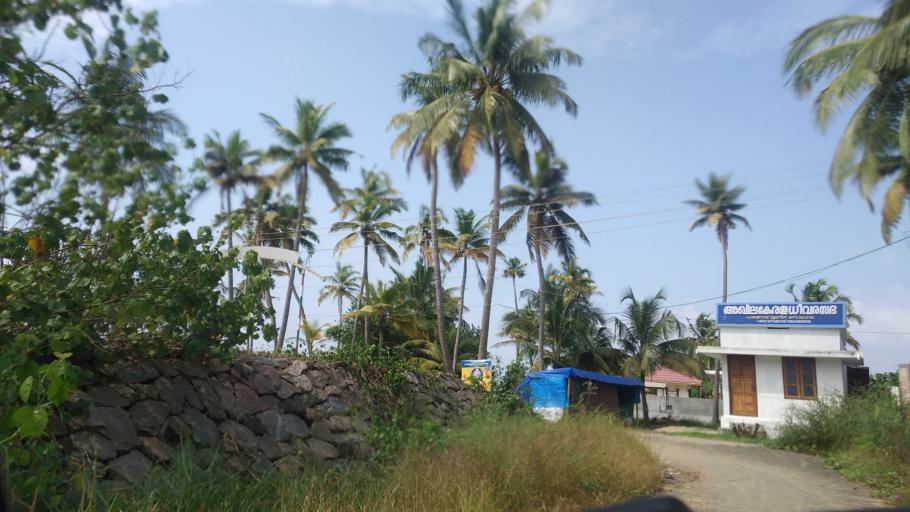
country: IN
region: Kerala
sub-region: Ernakulam
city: Elur
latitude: 10.0831
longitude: 76.1945
